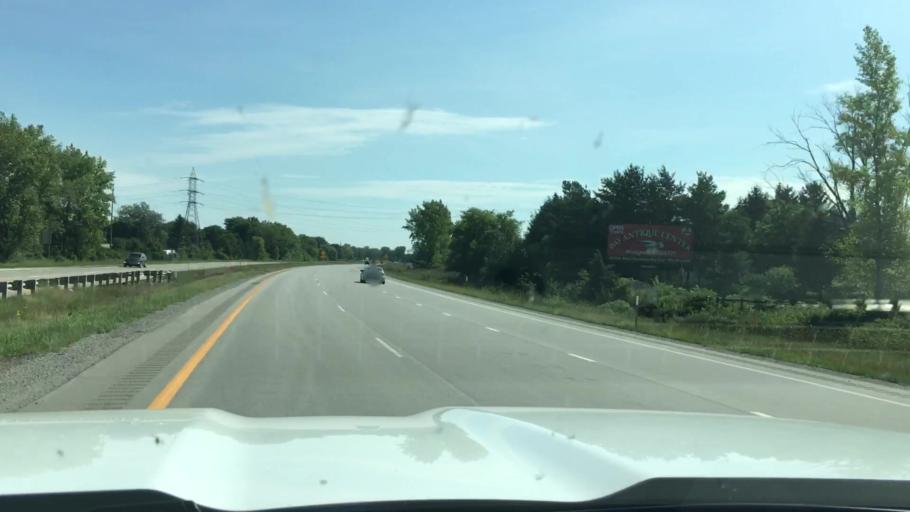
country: US
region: Michigan
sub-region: Bay County
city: Bay City
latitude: 43.5964
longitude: -83.9435
